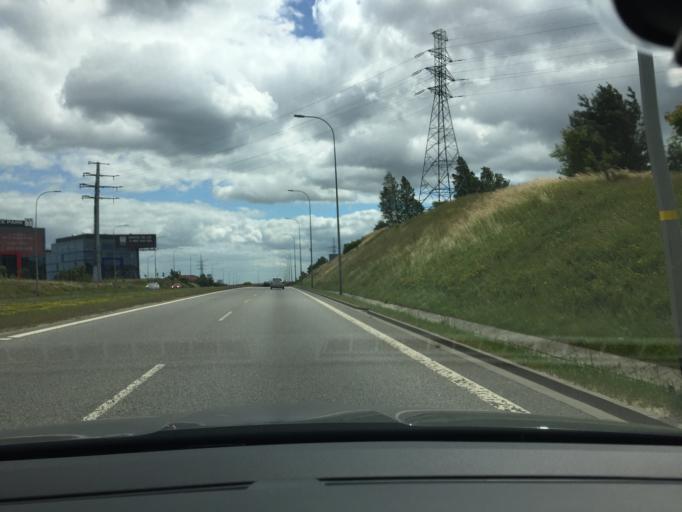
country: PL
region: Pomeranian Voivodeship
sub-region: Powiat gdanski
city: Kowale
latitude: 54.3399
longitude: 18.5521
